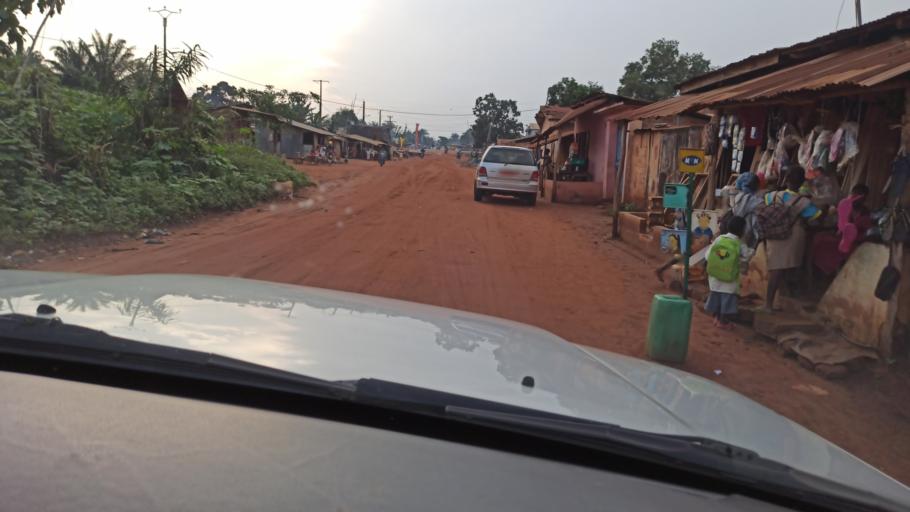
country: BJ
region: Queme
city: Porto-Novo
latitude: 6.5347
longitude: 2.6497
